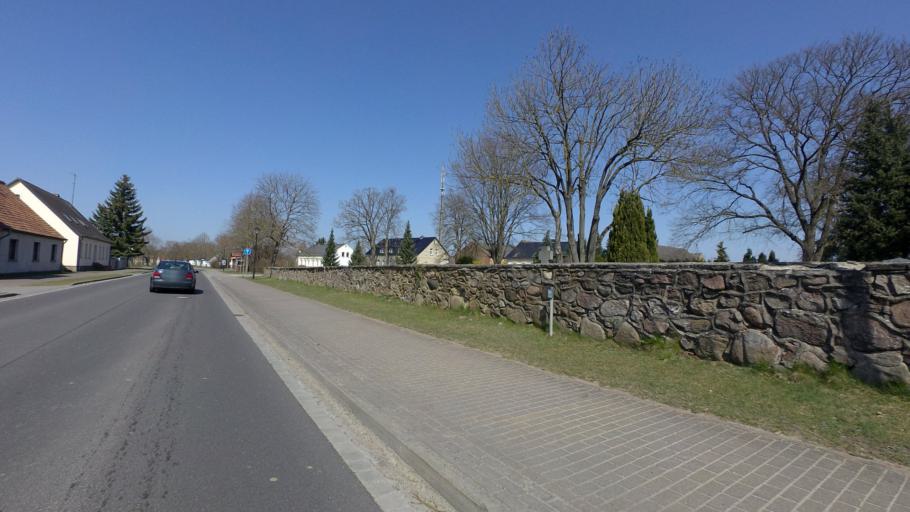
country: DE
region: Brandenburg
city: Ruthnick
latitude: 52.9039
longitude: 12.9687
